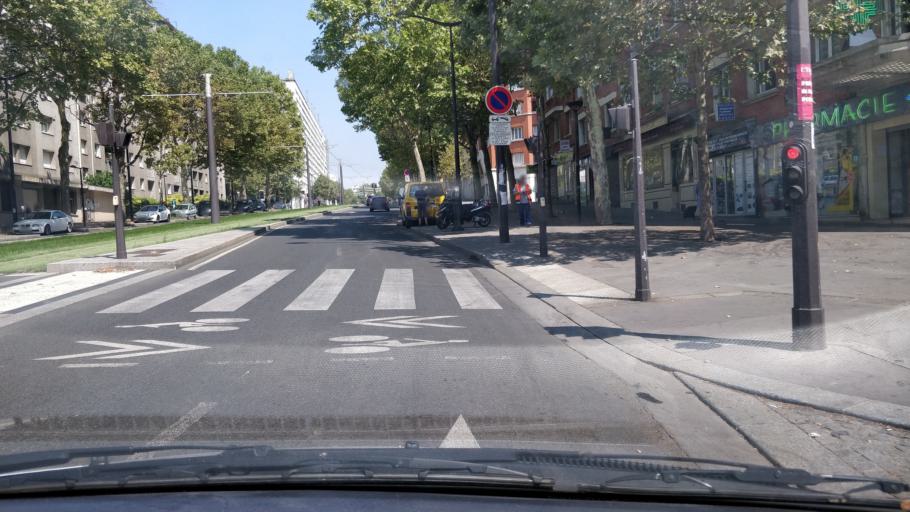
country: FR
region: Ile-de-France
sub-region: Departement de Seine-Saint-Denis
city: Bagnolet
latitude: 48.8691
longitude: 2.4090
